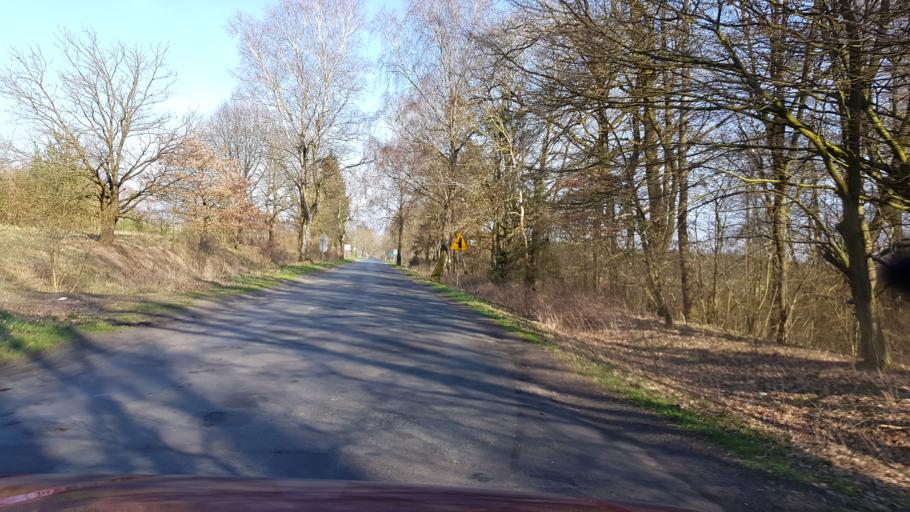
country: PL
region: West Pomeranian Voivodeship
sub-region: Powiat goleniowski
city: Nowogard
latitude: 53.6760
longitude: 15.2102
